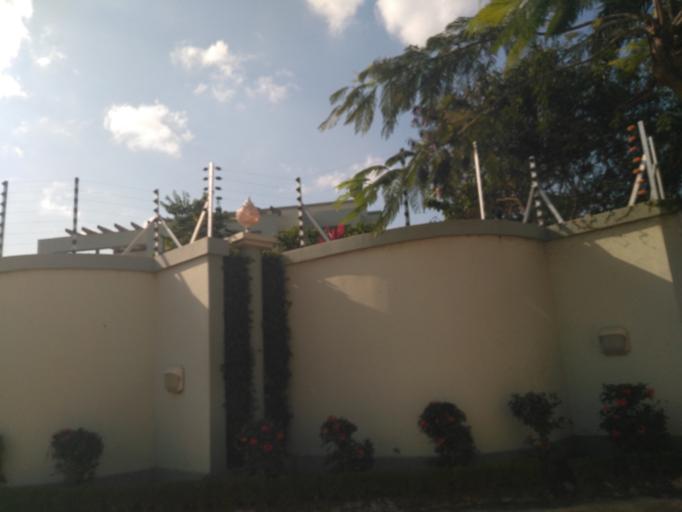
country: TZ
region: Dar es Salaam
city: Magomeni
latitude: -6.7697
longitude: 39.2547
